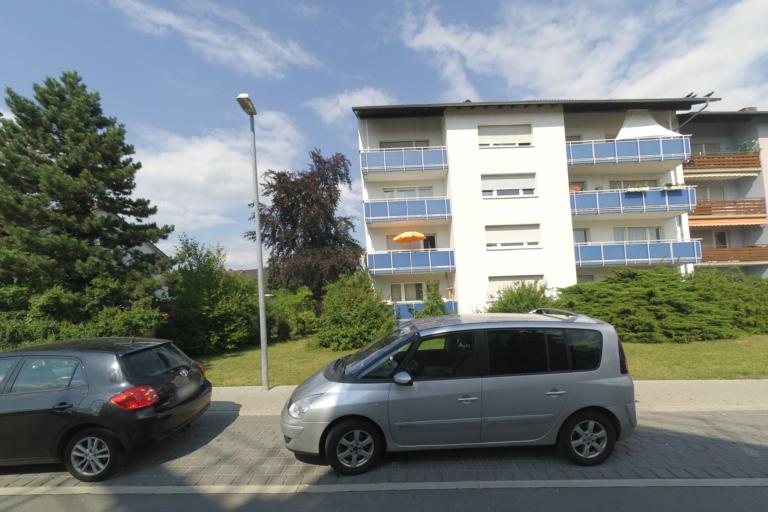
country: DE
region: Hesse
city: Viernheim
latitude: 49.5395
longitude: 8.5637
